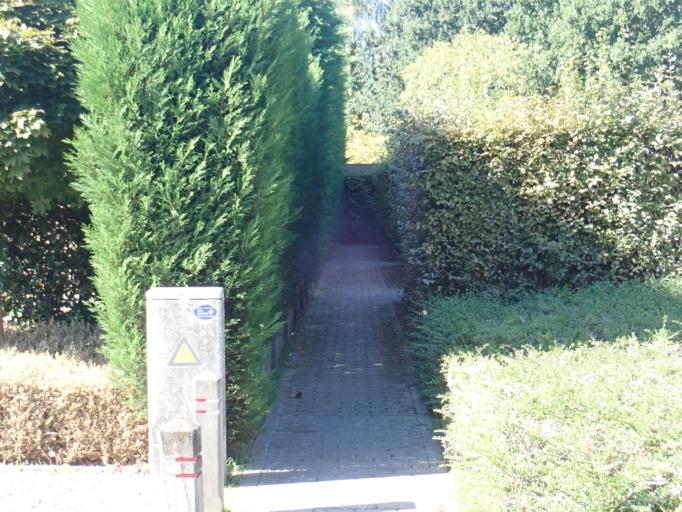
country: BE
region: Flanders
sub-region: Provincie Antwerpen
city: Kasterlee
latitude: 51.2222
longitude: 4.9187
